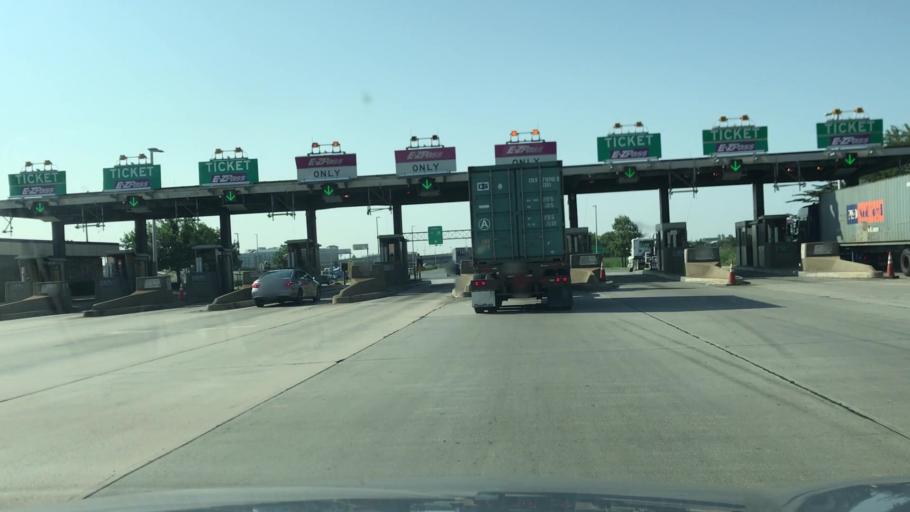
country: US
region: New Jersey
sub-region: Union County
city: Elizabeth
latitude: 40.6691
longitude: -74.1848
